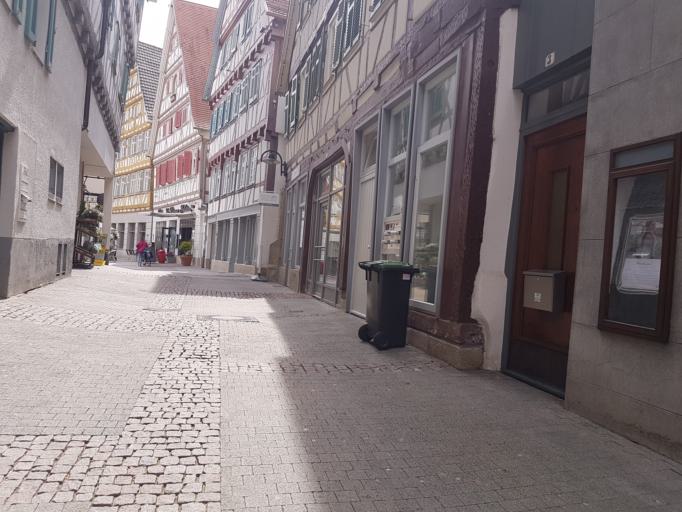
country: DE
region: Baden-Wuerttemberg
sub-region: Regierungsbezirk Stuttgart
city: Herrenberg
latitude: 48.5968
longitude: 8.8701
